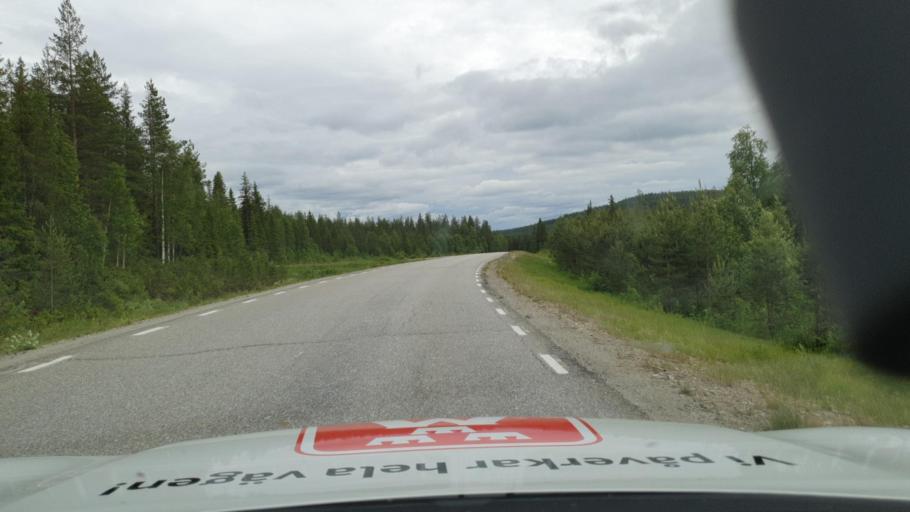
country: SE
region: Vaesterbotten
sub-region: Lycksele Kommun
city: Soderfors
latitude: 64.3213
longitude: 18.1562
